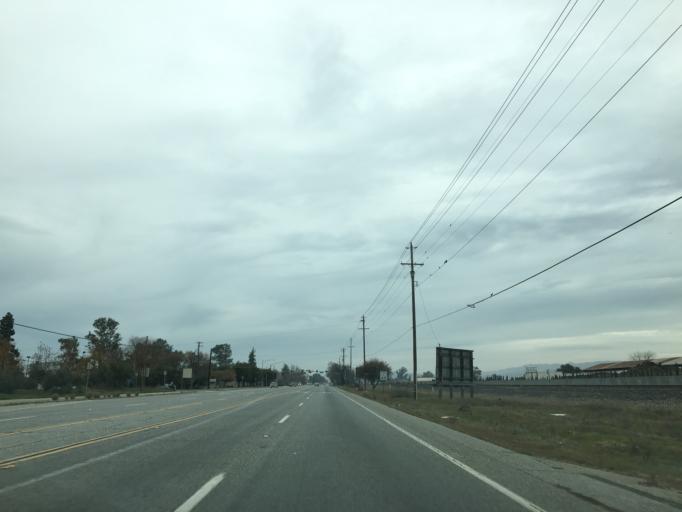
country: US
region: California
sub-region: Santa Clara County
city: San Martin
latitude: 37.0721
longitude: -121.6026
